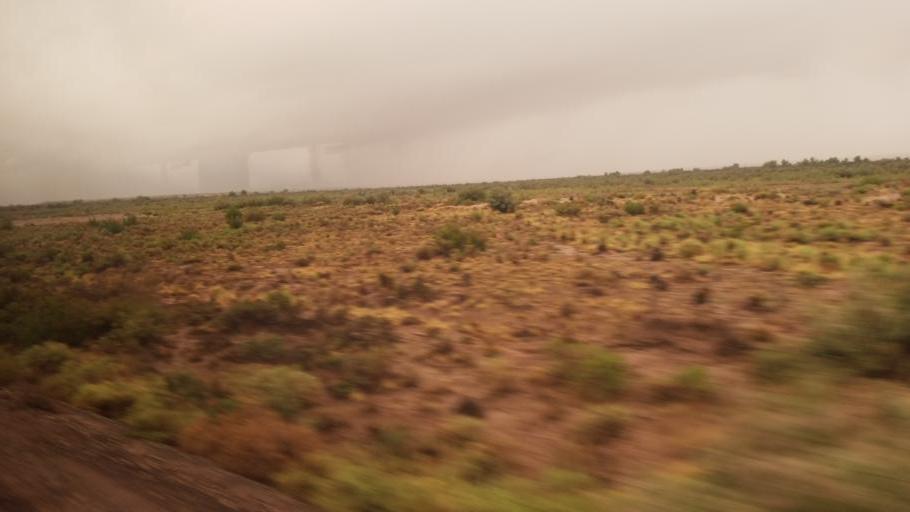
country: US
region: Arizona
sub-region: Navajo County
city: Joseph City
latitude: 34.9674
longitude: -110.4460
